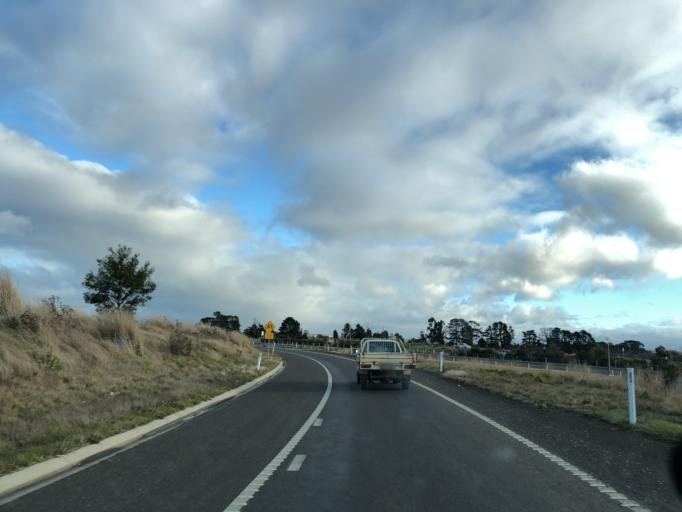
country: AU
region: Victoria
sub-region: Mount Alexander
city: Castlemaine
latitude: -37.1931
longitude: 144.4061
